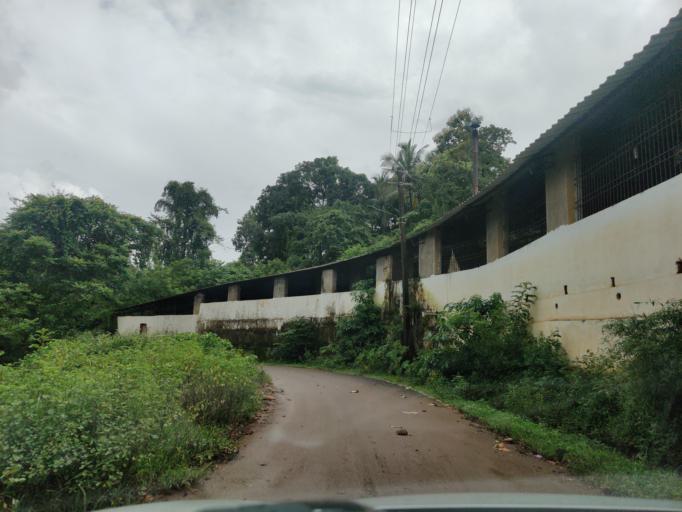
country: IN
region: Goa
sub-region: North Goa
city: Valpoy
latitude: 15.5323
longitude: 74.1407
